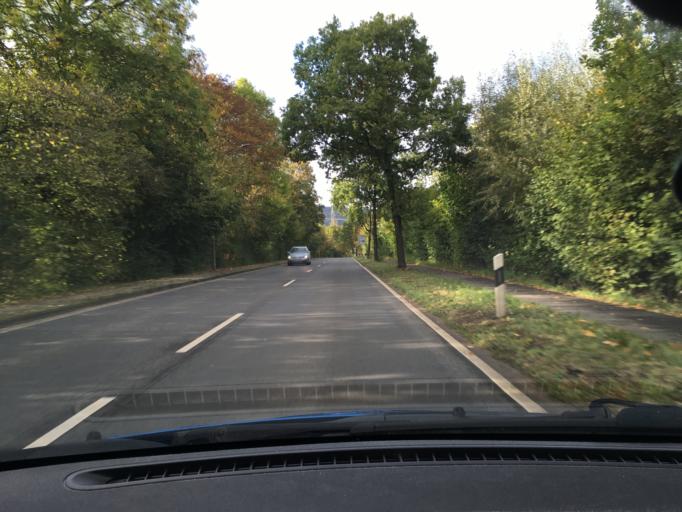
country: DE
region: Lower Saxony
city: Springe
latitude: 52.1957
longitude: 9.5598
